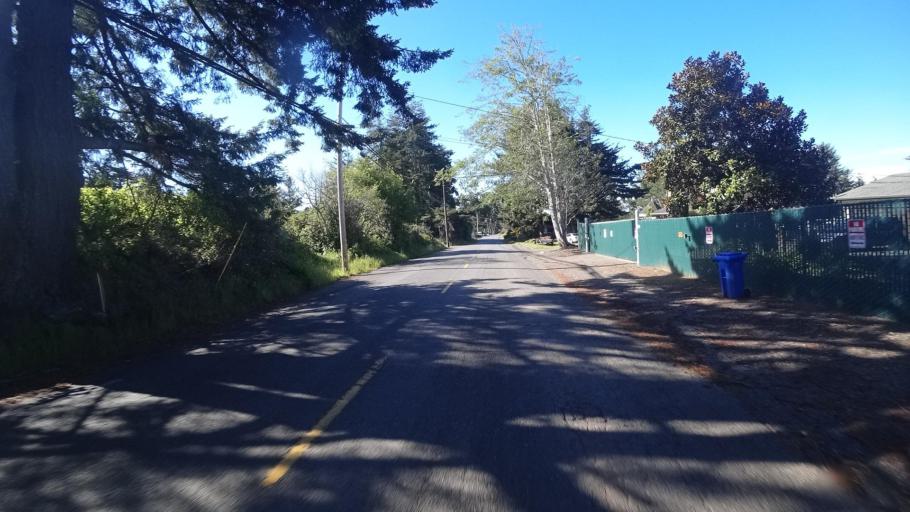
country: US
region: California
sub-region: Humboldt County
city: McKinleyville
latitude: 40.9654
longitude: -124.0960
